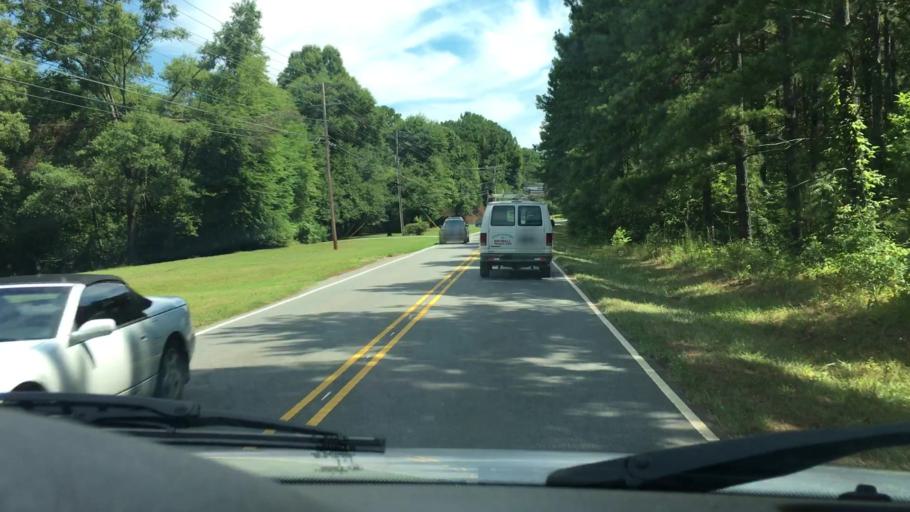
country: US
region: North Carolina
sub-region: Mecklenburg County
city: Huntersville
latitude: 35.4167
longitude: -80.9218
